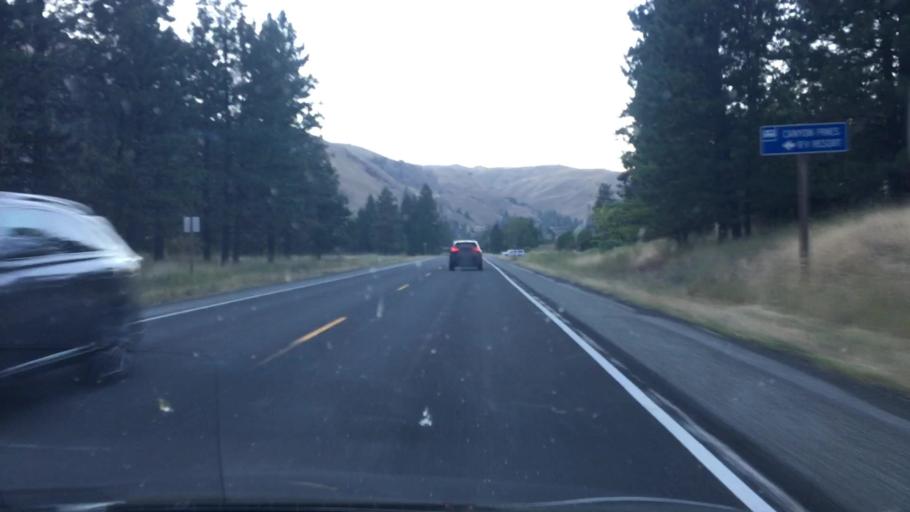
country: US
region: Idaho
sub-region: Valley County
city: McCall
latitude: 45.2915
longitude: -116.3567
